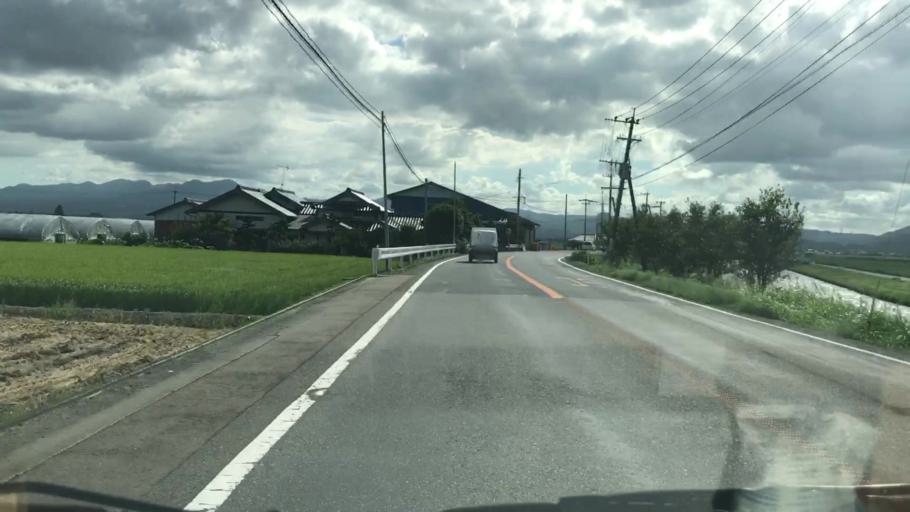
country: JP
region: Saga Prefecture
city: Kashima
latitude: 33.1585
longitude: 130.1627
